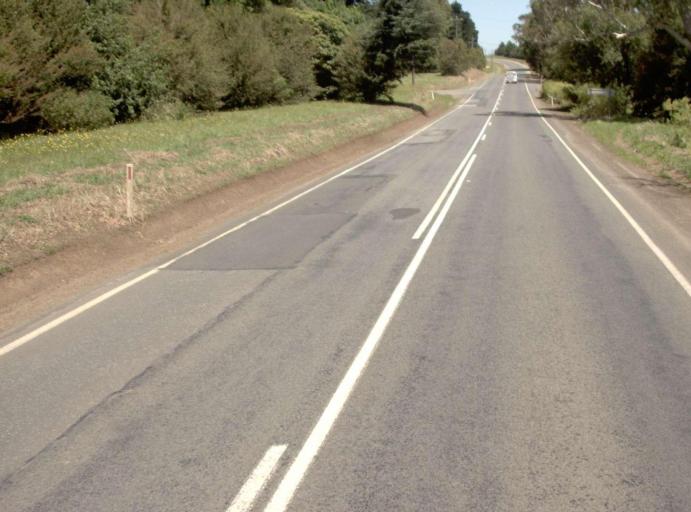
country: AU
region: Victoria
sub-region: Baw Baw
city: Warragul
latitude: -37.9774
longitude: 145.9459
